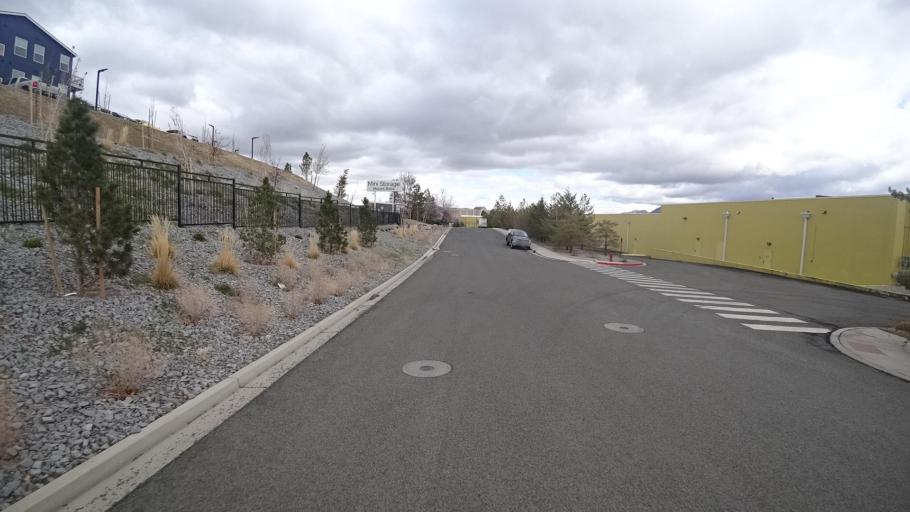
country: US
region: Nevada
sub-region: Washoe County
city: Sparks
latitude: 39.4020
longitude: -119.7527
